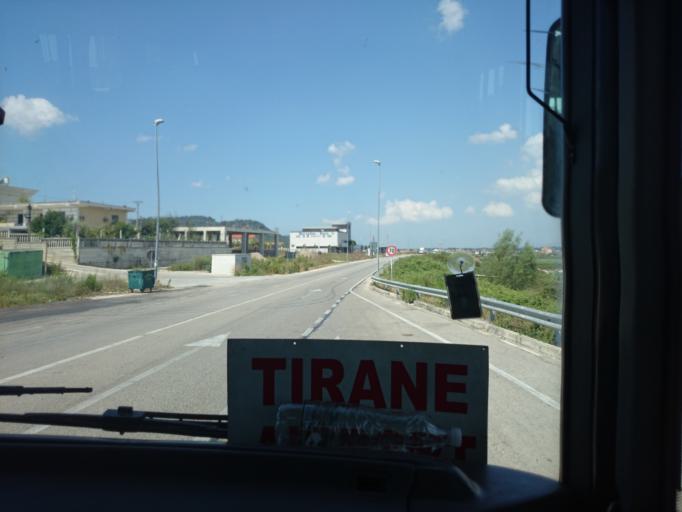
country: AL
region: Tirane
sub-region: Rrethi i Tiranes
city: Kashar
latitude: 41.3681
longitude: 19.7040
